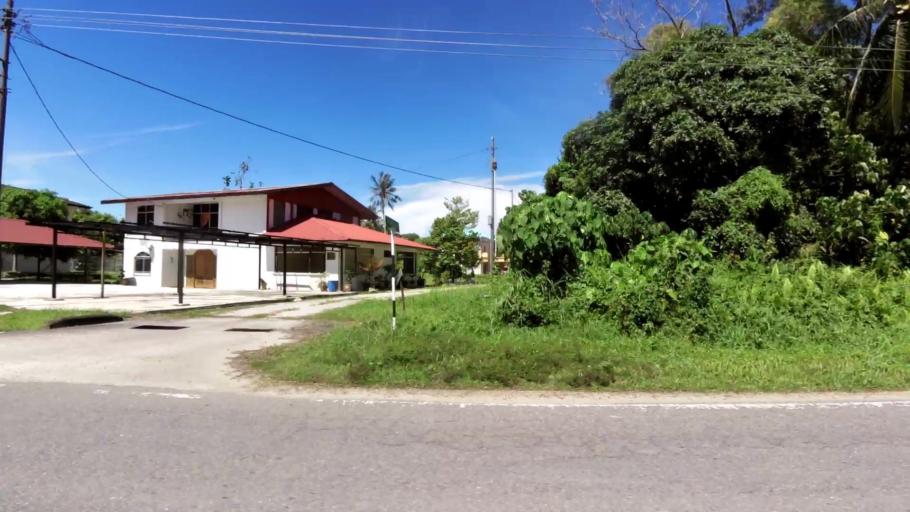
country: BN
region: Brunei and Muara
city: Bandar Seri Begawan
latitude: 5.0150
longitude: 115.0579
